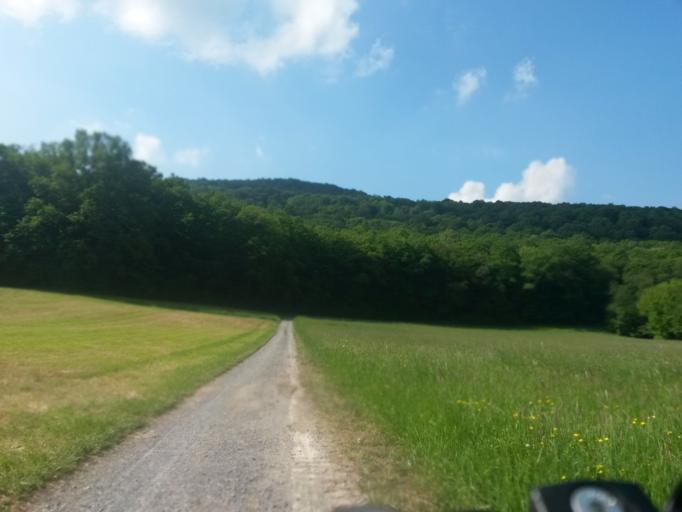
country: DE
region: Bavaria
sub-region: Regierungsbezirk Unterfranken
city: Ramsthal
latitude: 50.1680
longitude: 10.0630
